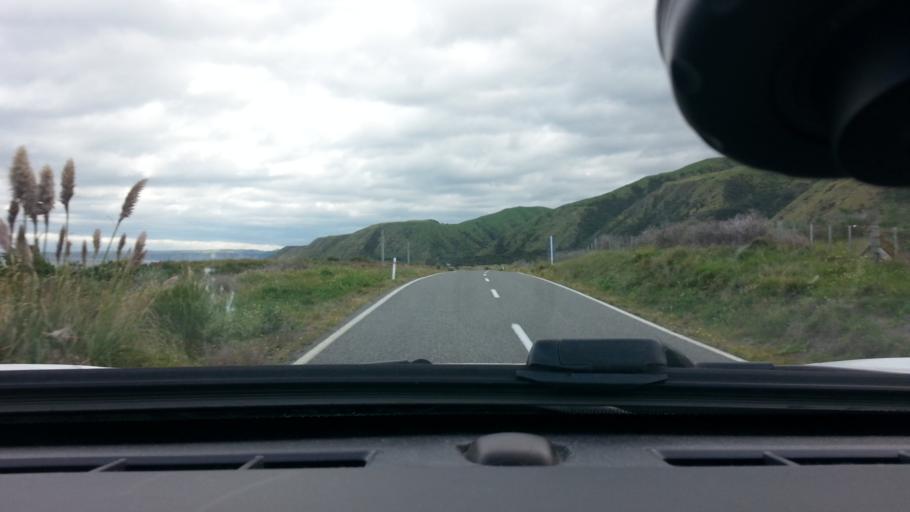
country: NZ
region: Wellington
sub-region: South Wairarapa District
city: Waipawa
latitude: -41.5084
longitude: 175.2053
